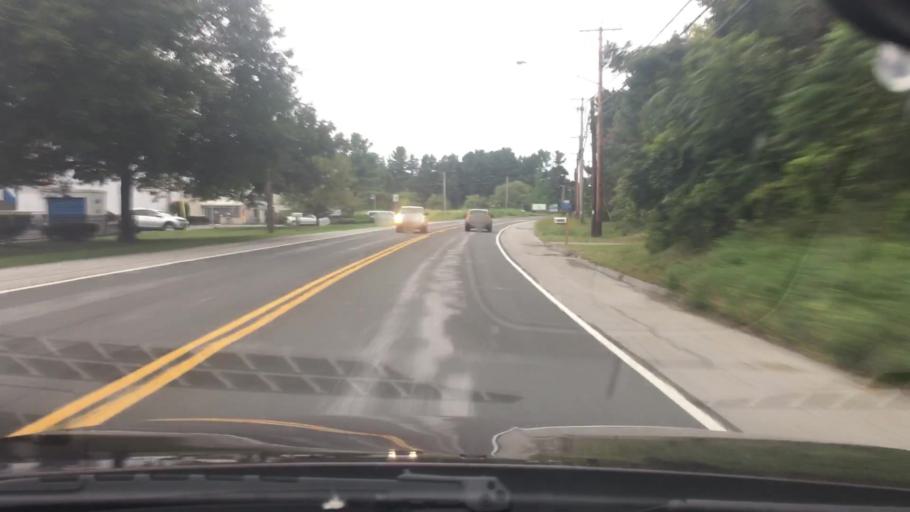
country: US
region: New York
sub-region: Dutchess County
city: Pleasant Valley
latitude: 41.7269
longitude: -73.8413
